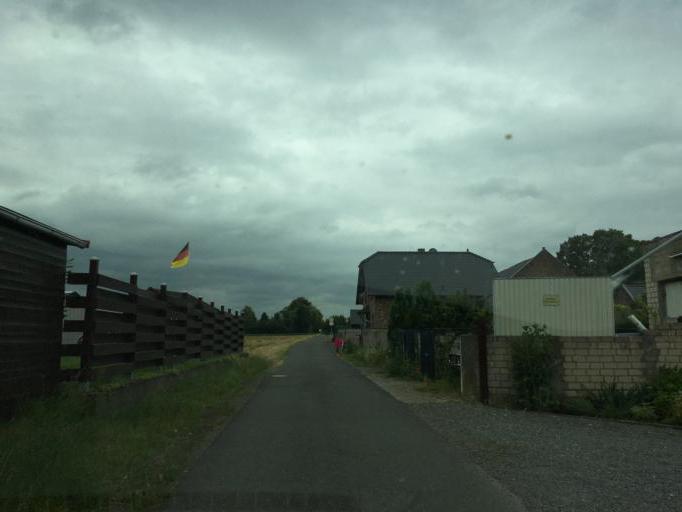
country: DE
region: North Rhine-Westphalia
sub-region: Regierungsbezirk Koln
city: Merzenich
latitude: 50.7963
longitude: 6.5428
